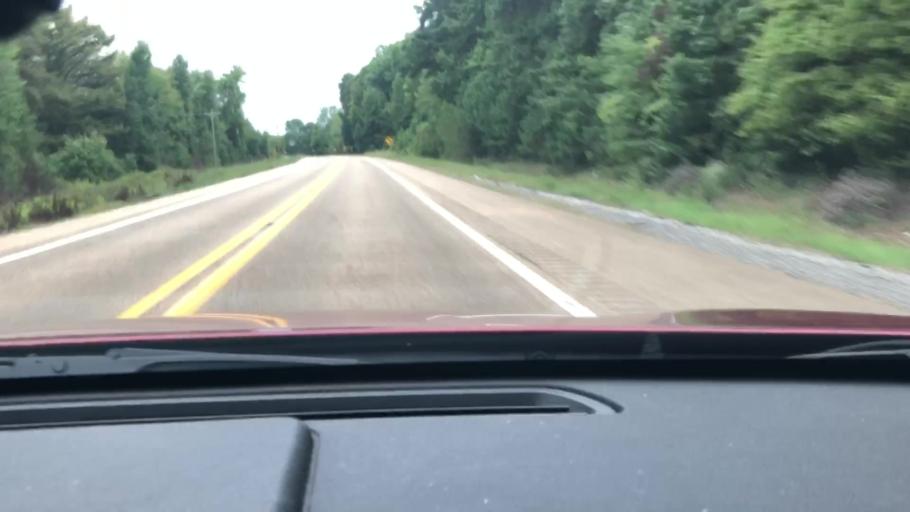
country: US
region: Arkansas
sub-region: Miller County
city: Texarkana
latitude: 33.4161
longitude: -93.8118
